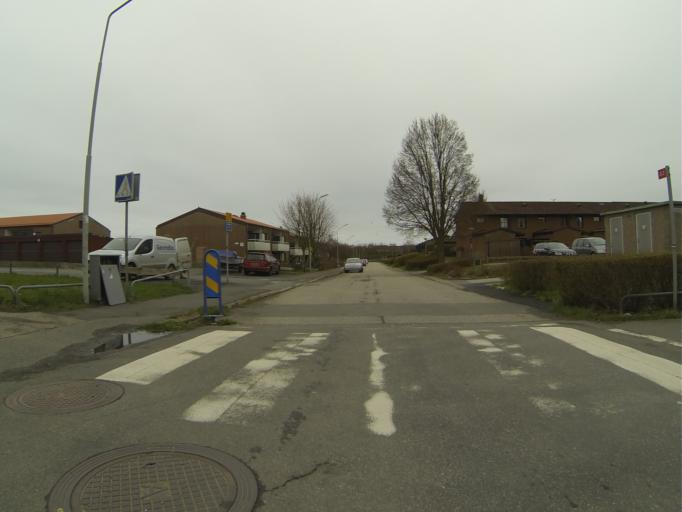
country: SE
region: Skane
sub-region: Simrishamns Kommun
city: Simrishamn
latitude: 55.5458
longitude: 14.3438
